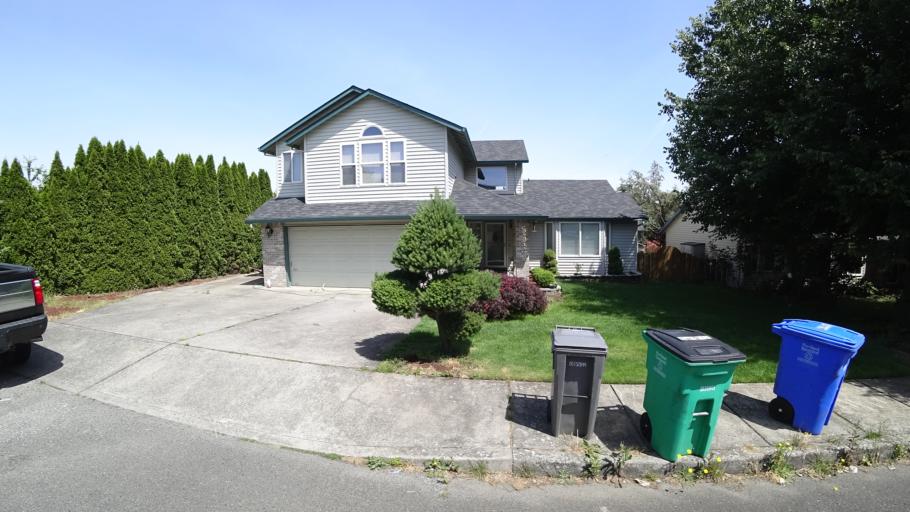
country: US
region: Oregon
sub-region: Multnomah County
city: Fairview
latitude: 45.5504
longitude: -122.5092
